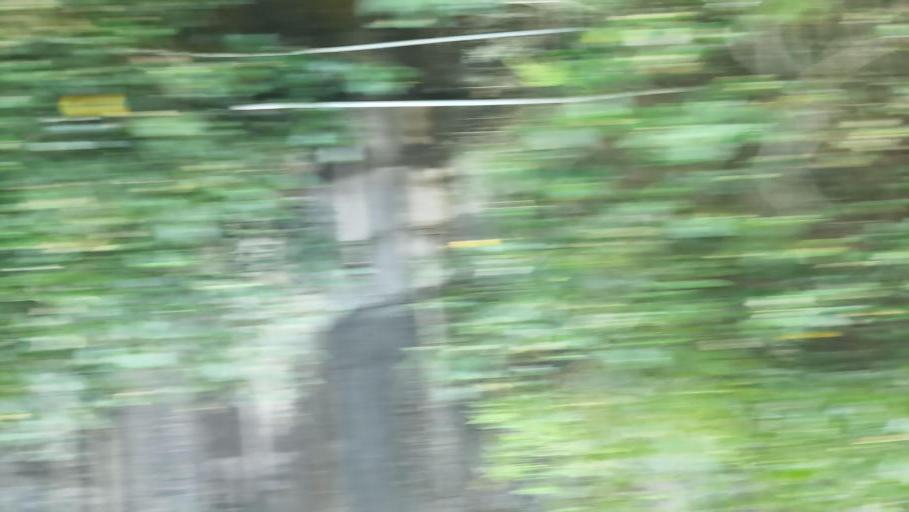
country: TW
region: Taipei
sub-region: Taipei
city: Banqiao
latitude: 24.8929
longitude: 121.4253
